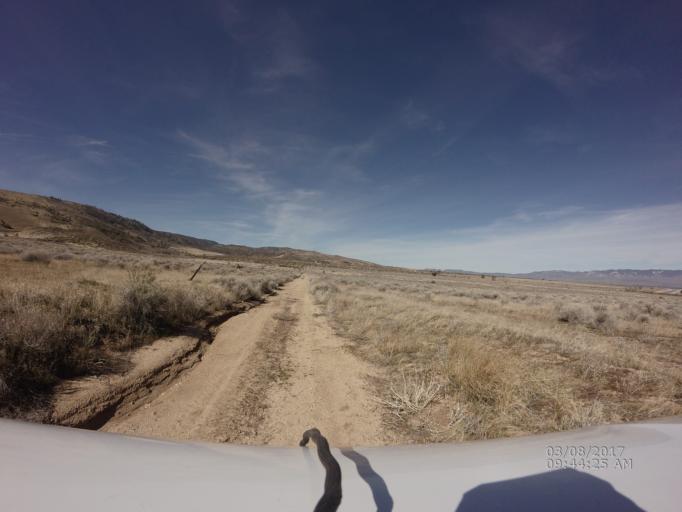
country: US
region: California
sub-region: Los Angeles County
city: Green Valley
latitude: 34.7311
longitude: -118.4769
